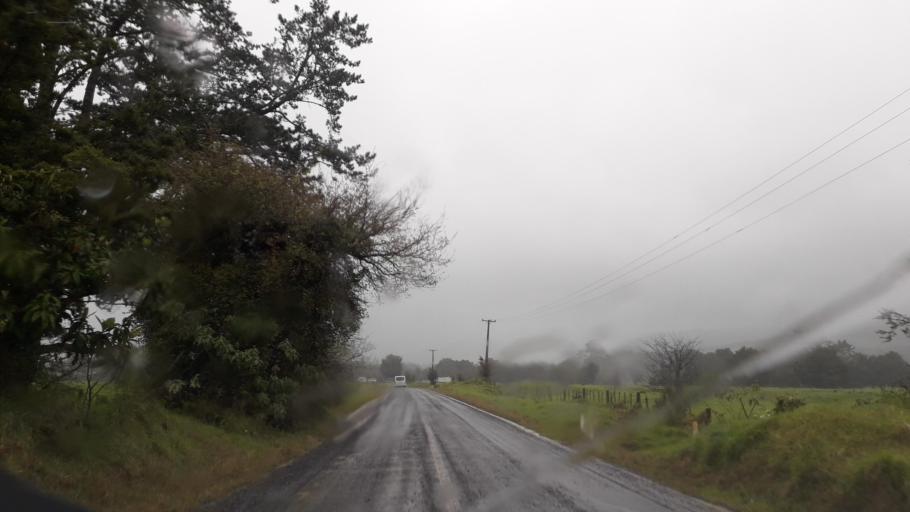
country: NZ
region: Northland
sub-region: Far North District
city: Waimate North
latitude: -35.4994
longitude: 173.6988
